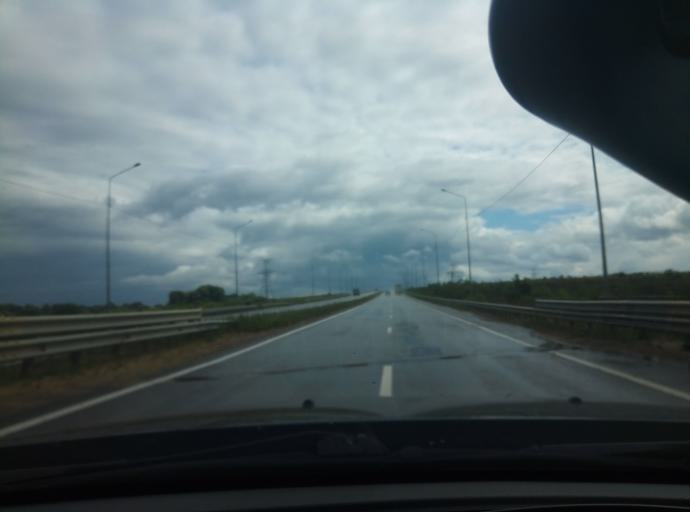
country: RU
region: Tula
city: Kamenetskiy
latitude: 54.0361
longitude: 38.2098
